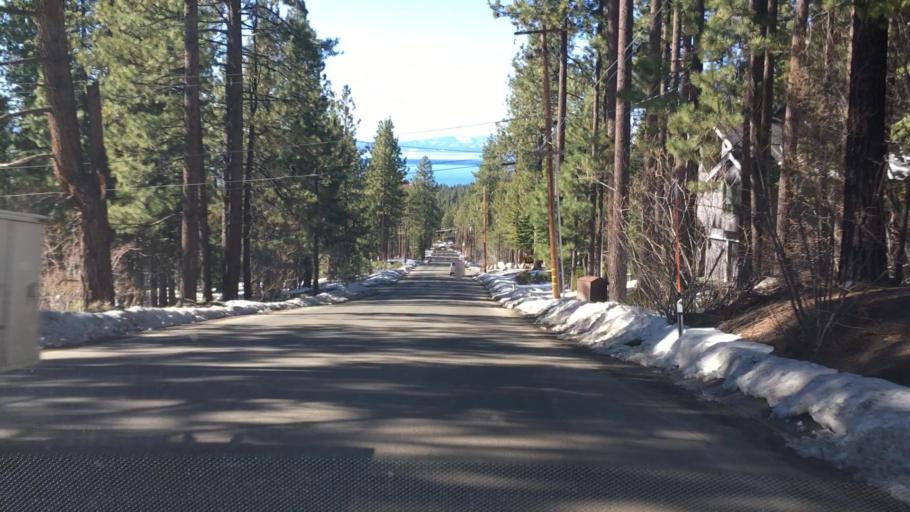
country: US
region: California
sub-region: El Dorado County
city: South Lake Tahoe
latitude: 38.9423
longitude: -119.9417
